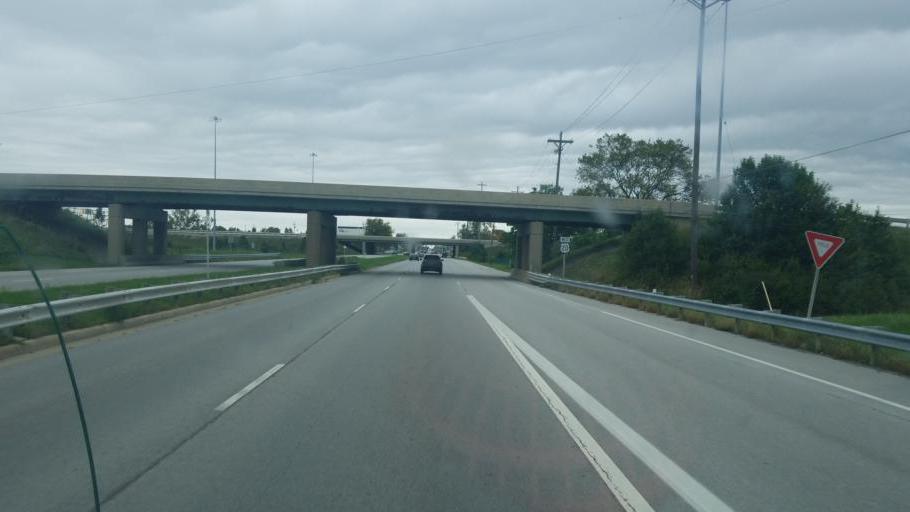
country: US
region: Ohio
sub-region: Lucas County
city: Maumee
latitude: 41.5895
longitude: -83.6647
